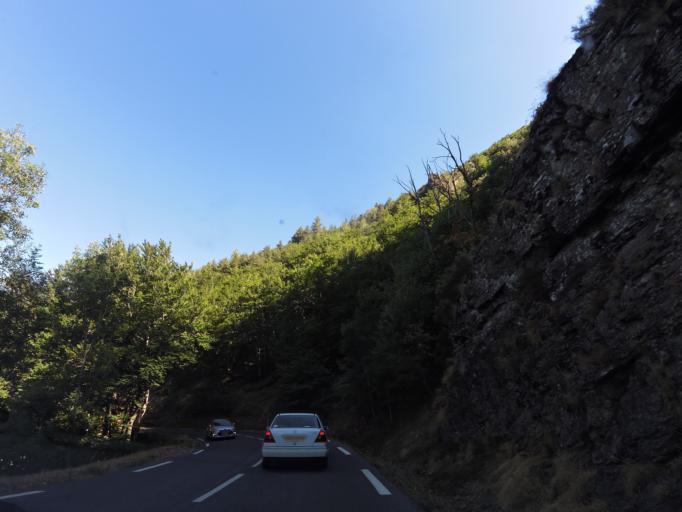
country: FR
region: Languedoc-Roussillon
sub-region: Departement du Gard
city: Valleraugue
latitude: 44.0853
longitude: 3.5774
